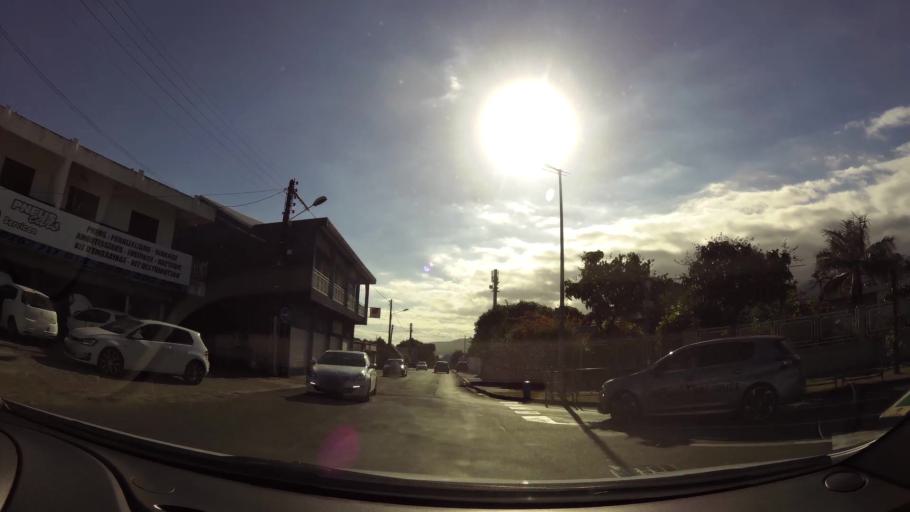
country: RE
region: Reunion
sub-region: Reunion
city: Saint-Louis
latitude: -21.2861
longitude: 55.4134
